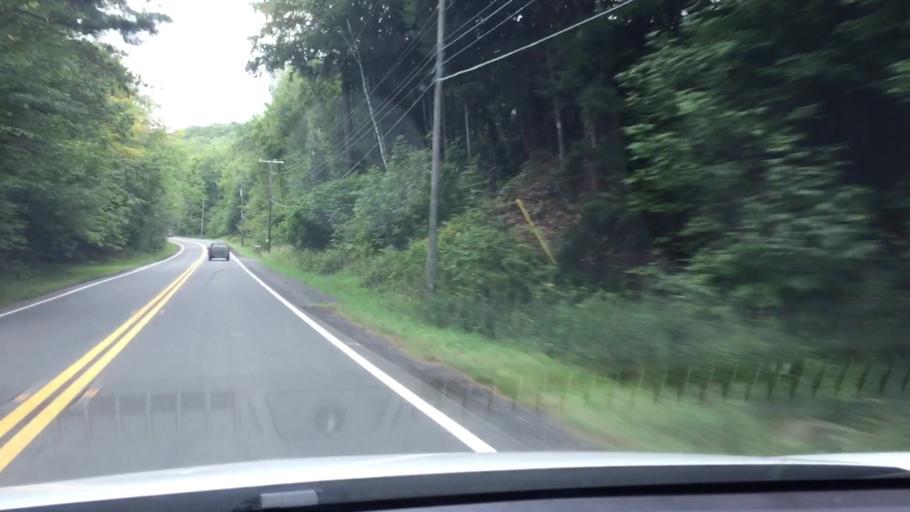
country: US
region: Massachusetts
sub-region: Berkshire County
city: Hinsdale
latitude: 42.3827
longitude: -73.1224
